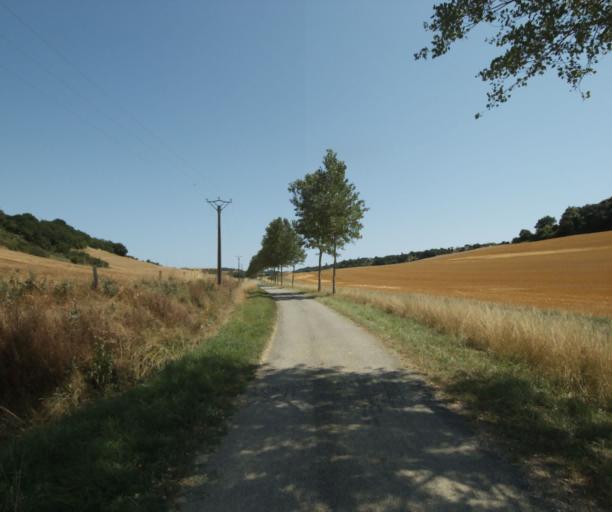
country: FR
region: Midi-Pyrenees
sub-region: Departement de la Haute-Garonne
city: Saint-Felix-Lauragais
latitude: 43.4620
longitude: 1.8634
